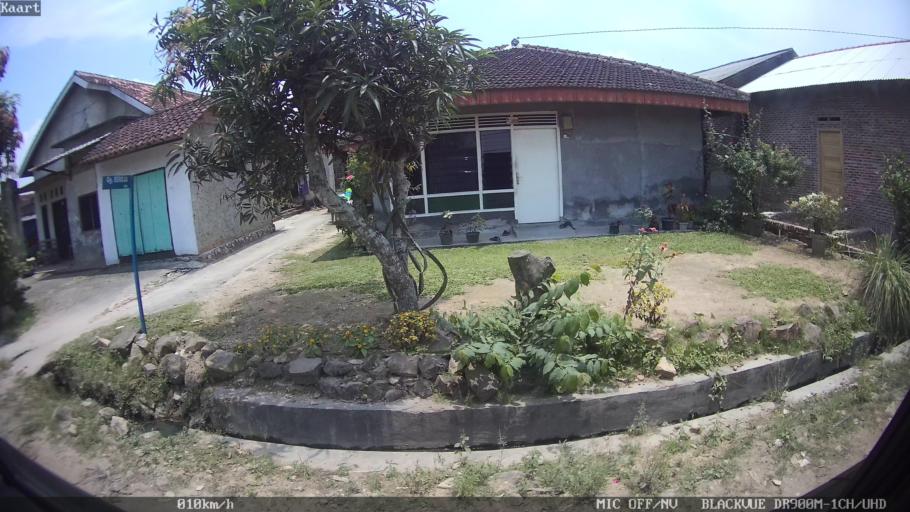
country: ID
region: Lampung
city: Kedaton
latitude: -5.3360
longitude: 105.2472
